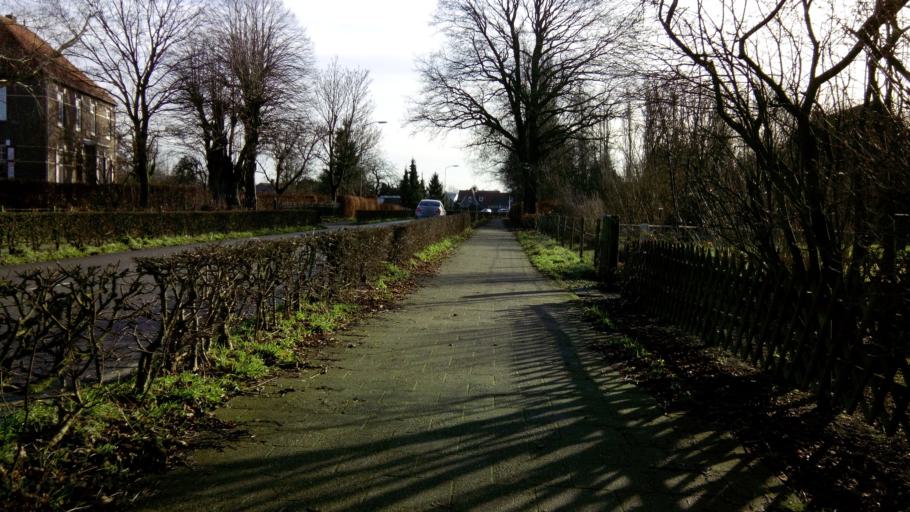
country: NL
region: Gelderland
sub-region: Gemeente Nijmegen
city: Nijmegen
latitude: 51.7918
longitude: 5.8408
